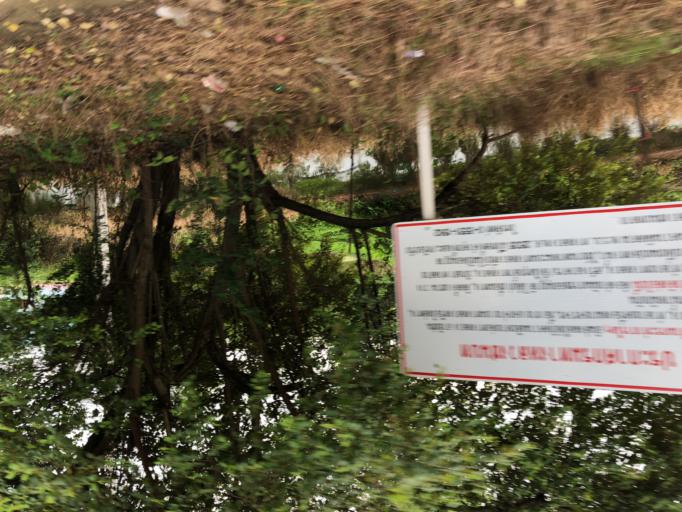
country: TH
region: Tak
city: Wang Chao
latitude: 16.6588
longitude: 99.2357
